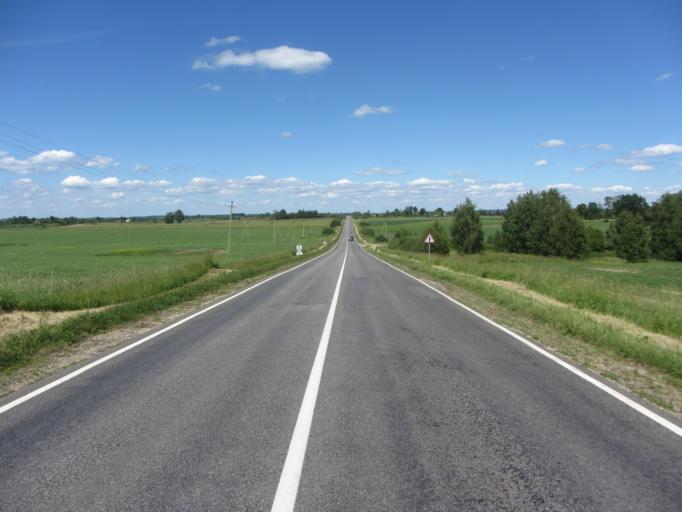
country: LT
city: Jieznas
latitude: 54.6525
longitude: 24.1849
